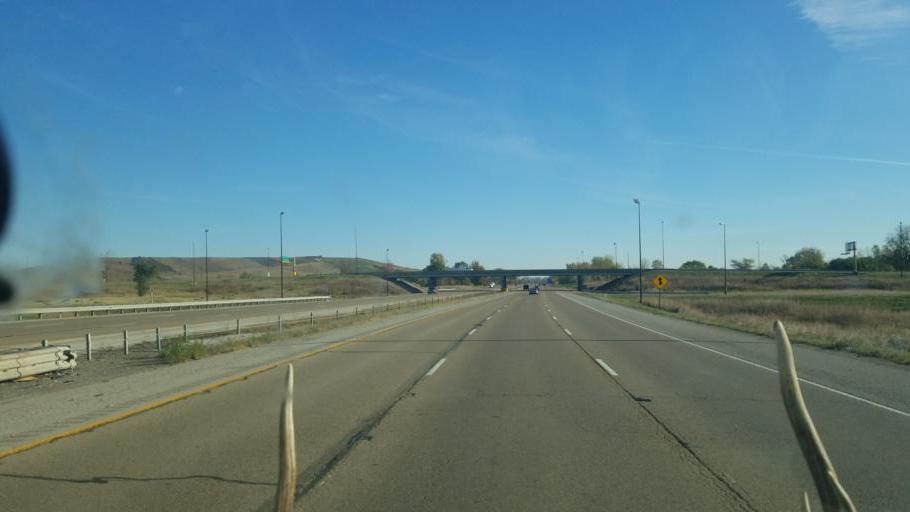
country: US
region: Illinois
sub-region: Saint Clair County
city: East Saint Louis
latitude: 38.6437
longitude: -90.1305
